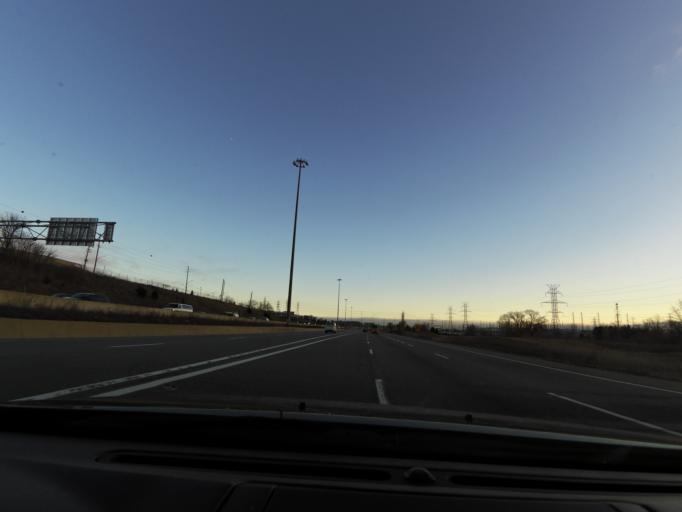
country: CA
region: Ontario
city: Burlington
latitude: 43.3289
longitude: -79.8417
